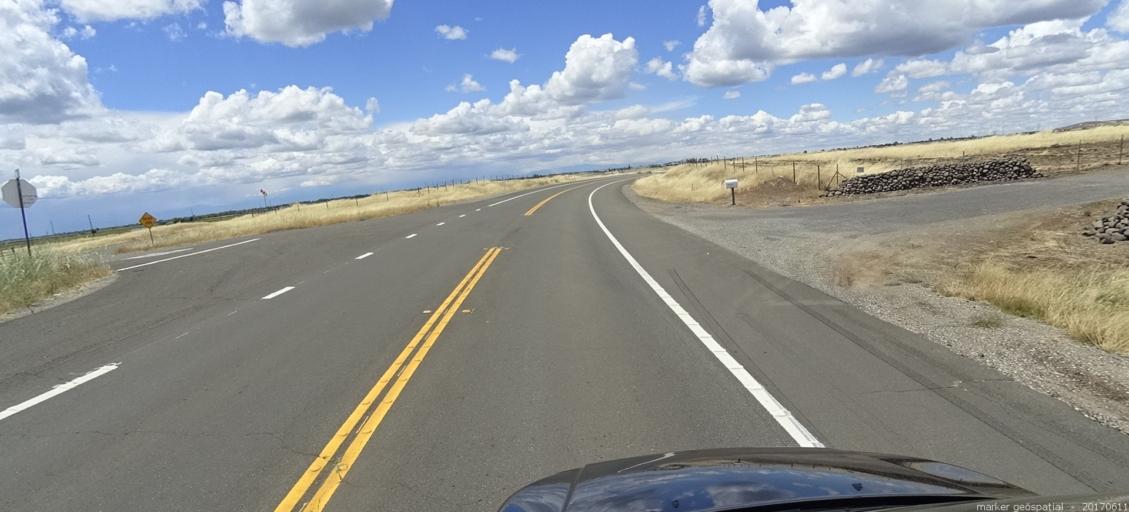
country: US
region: California
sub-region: Butte County
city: Durham
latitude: 39.6394
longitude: -121.7062
